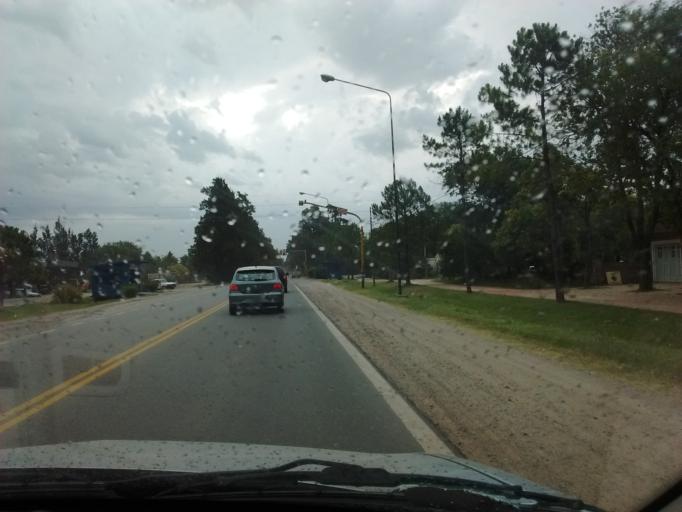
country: AR
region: Santa Fe
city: Funes
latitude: -32.9230
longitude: -60.7989
